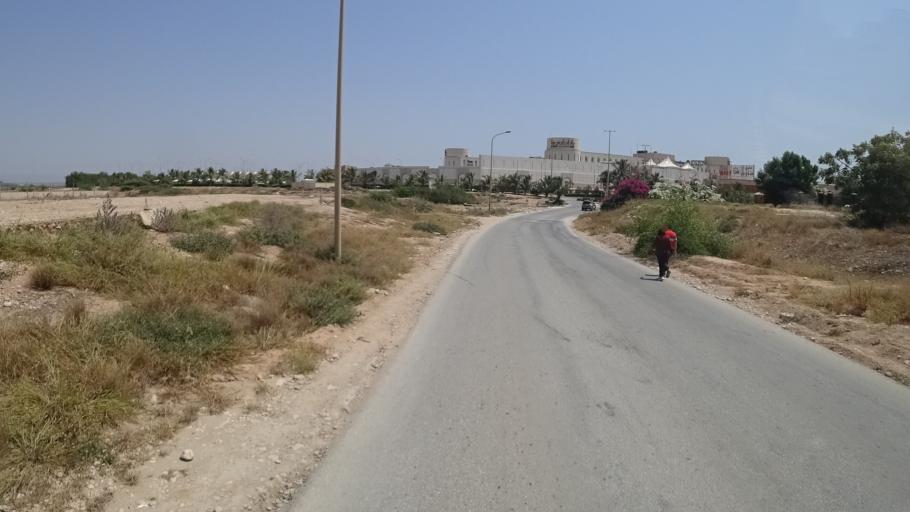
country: OM
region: Zufar
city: Salalah
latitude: 17.0238
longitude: 54.0625
